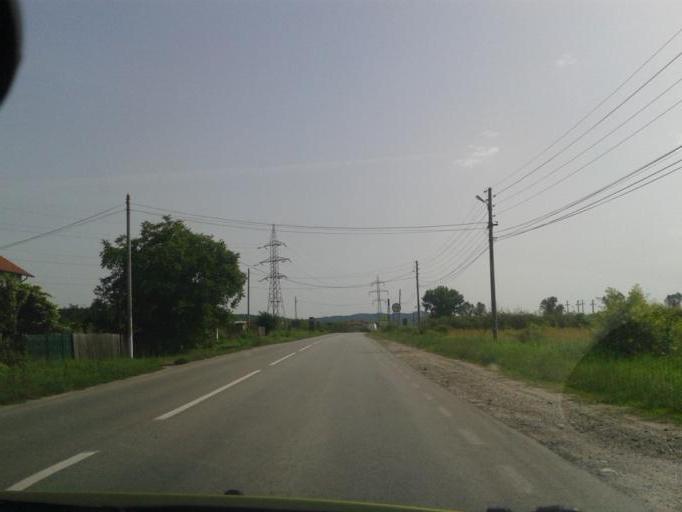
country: RO
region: Valcea
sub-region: Comuna Mihaesti
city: Mihaesti
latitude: 45.0489
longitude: 24.2752
